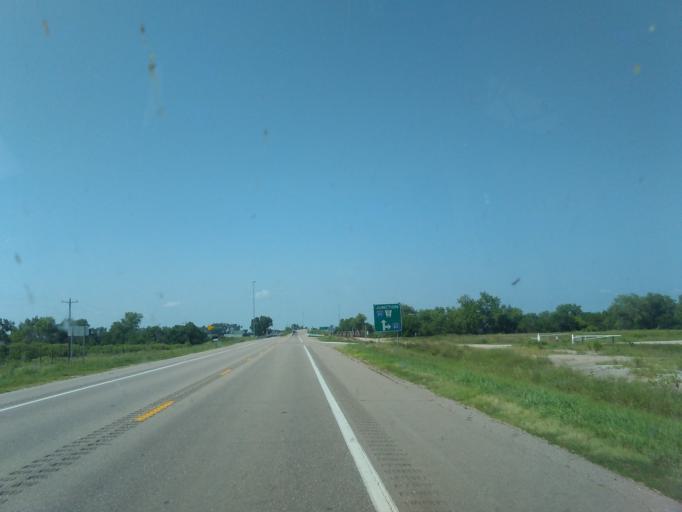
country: US
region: Nebraska
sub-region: Buffalo County
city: Gibbon
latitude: 40.6814
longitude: -98.9515
